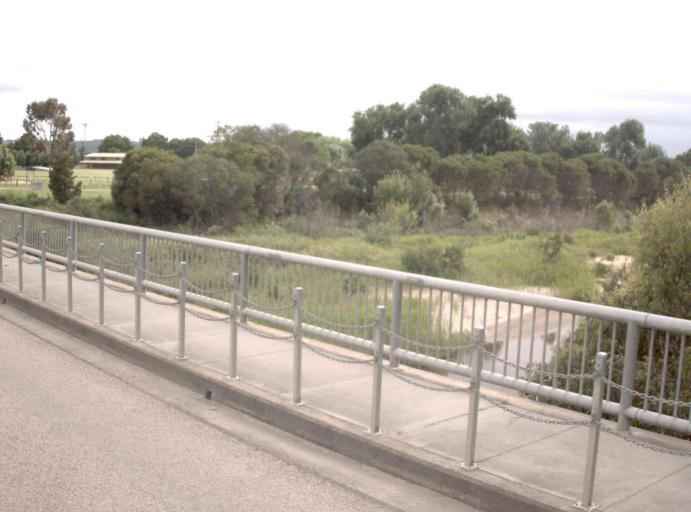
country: AU
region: Victoria
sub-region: East Gippsland
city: Lakes Entrance
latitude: -37.7105
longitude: 147.8359
